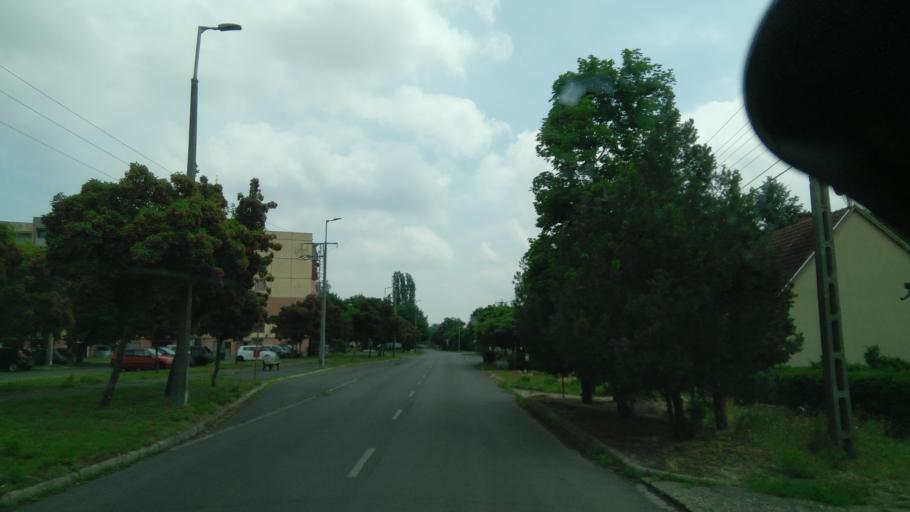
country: HU
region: Bekes
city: Gyula
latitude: 46.6548
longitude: 21.2625
